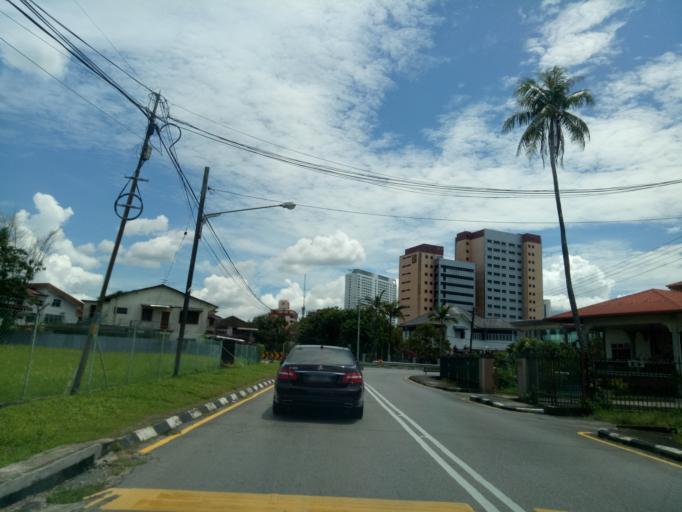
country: MY
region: Sarawak
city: Kuching
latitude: 1.5505
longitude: 110.3543
